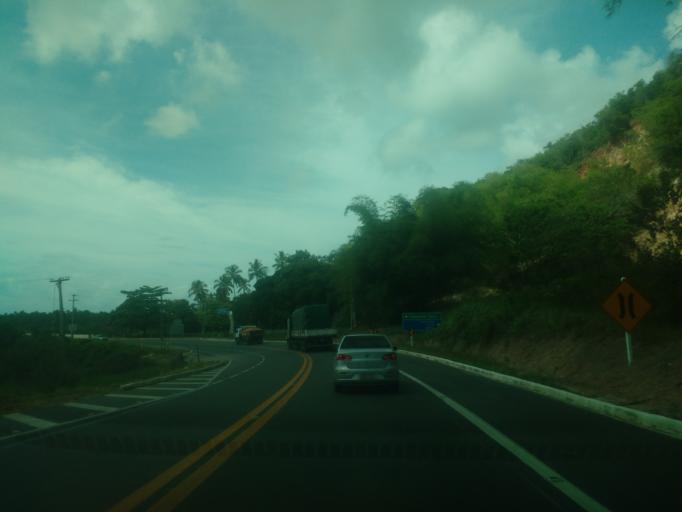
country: BR
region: Alagoas
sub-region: Marechal Deodoro
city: Marechal Deodoro
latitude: -9.6924
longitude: -35.8165
